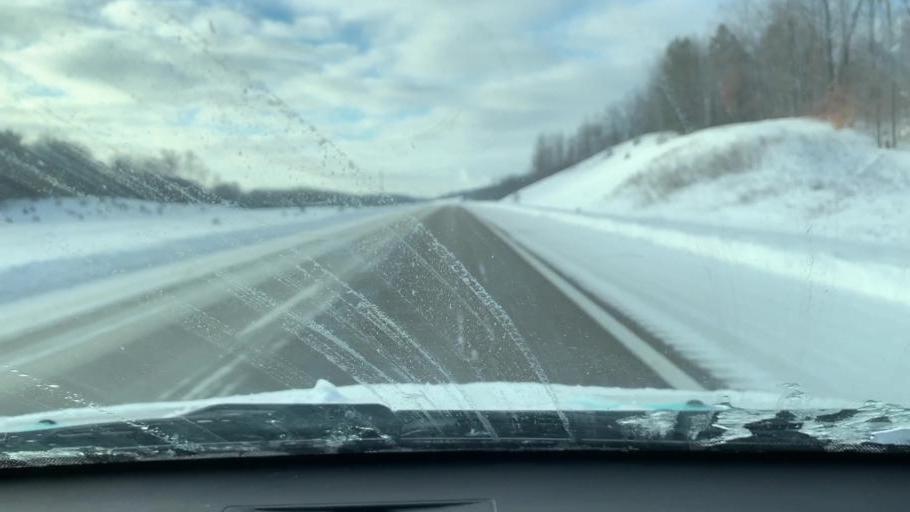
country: US
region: Michigan
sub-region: Wexford County
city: Manton
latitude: 44.3503
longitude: -85.4045
